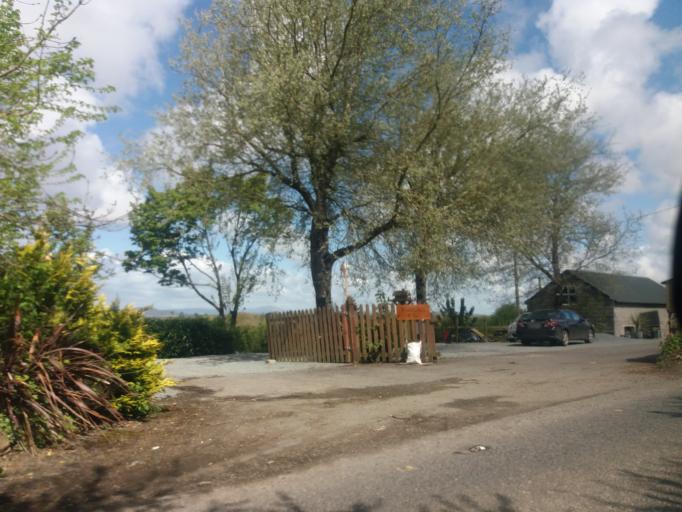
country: IE
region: Leinster
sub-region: Loch Garman
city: New Ross
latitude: 52.2803
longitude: -6.7202
